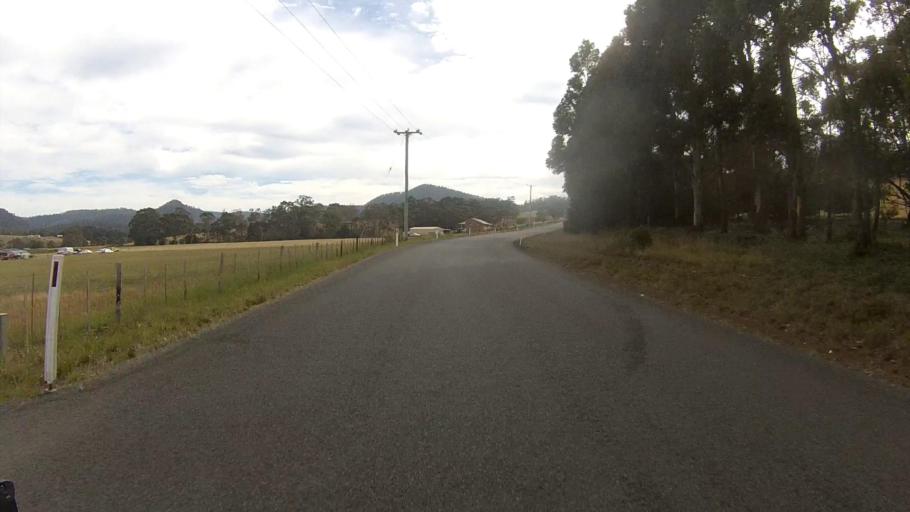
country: AU
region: Tasmania
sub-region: Sorell
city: Sorell
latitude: -42.7909
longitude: 147.8002
